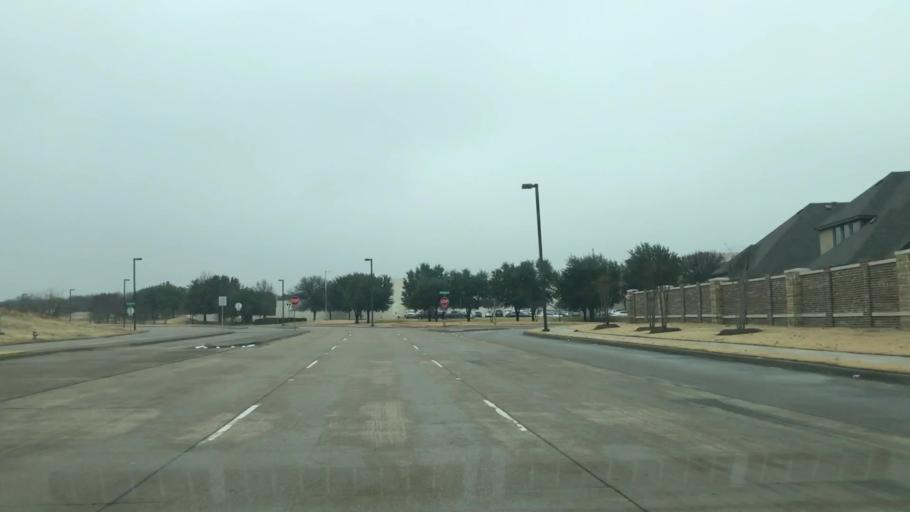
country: US
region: Texas
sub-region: Dallas County
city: Farmers Branch
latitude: 32.8853
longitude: -96.9405
